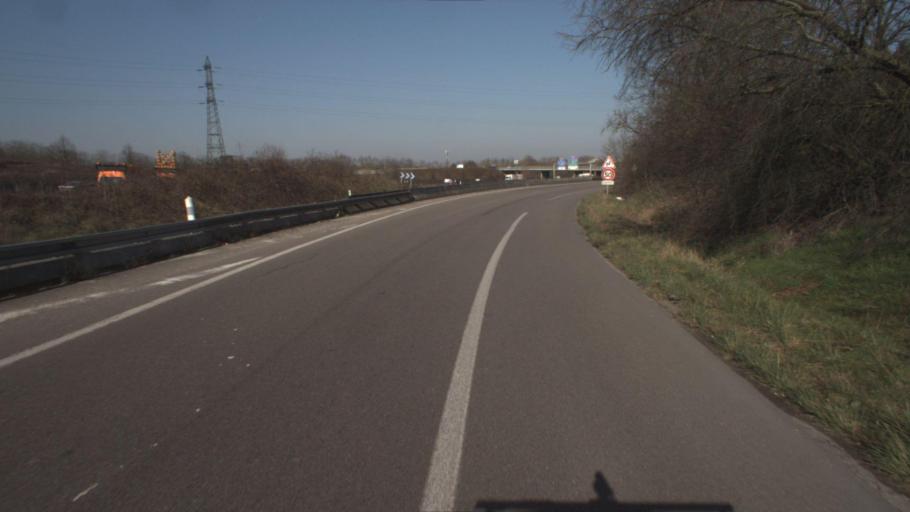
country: FR
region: Ile-de-France
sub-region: Departement de l'Essonne
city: Lisses
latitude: 48.6090
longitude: 2.4356
